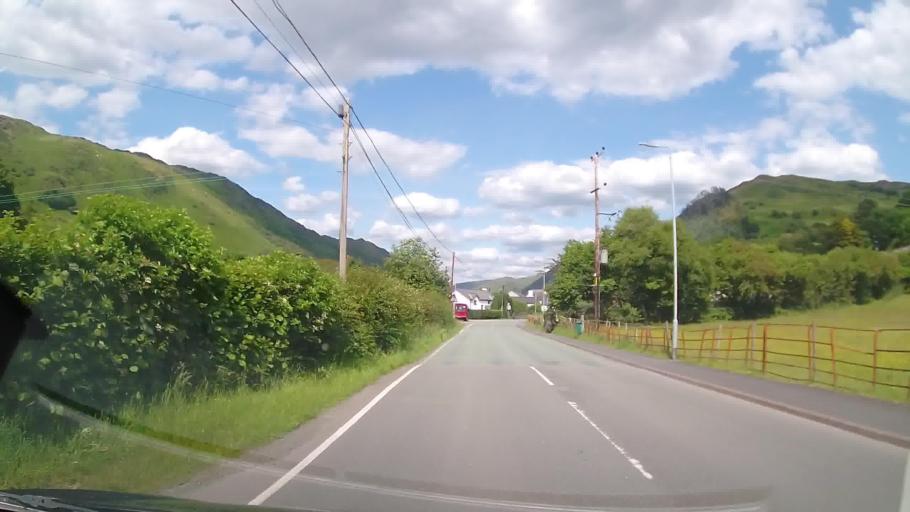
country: GB
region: Wales
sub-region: Gwynedd
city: Corris
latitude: 52.6432
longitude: -3.9591
